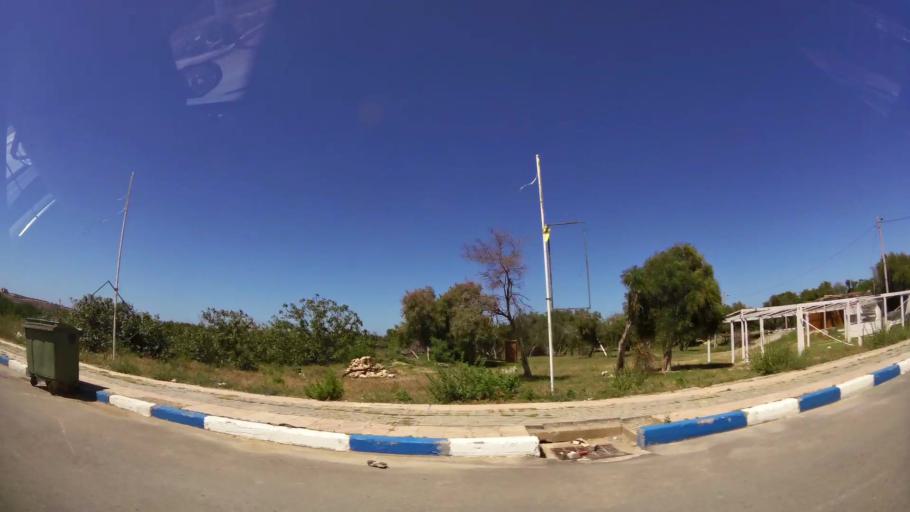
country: MA
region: Oriental
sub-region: Berkane-Taourirt
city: Madagh
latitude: 35.1367
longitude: -2.4150
